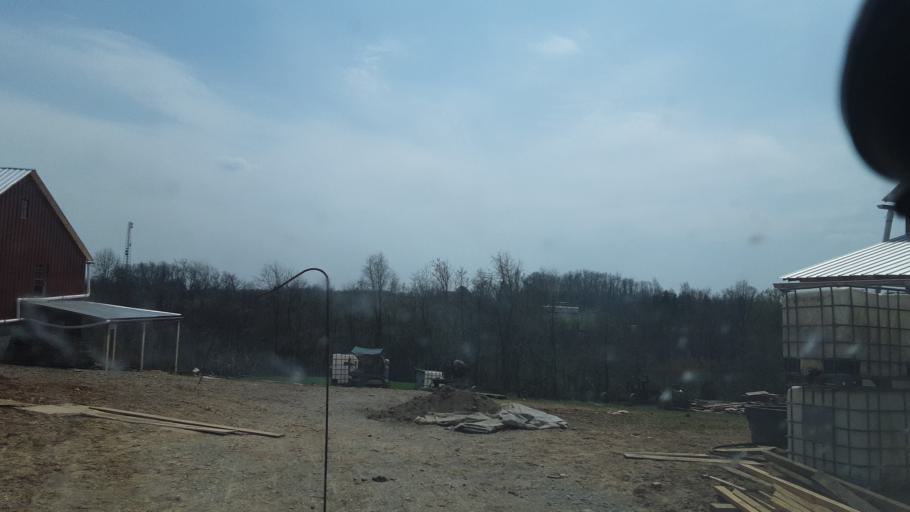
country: US
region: Ohio
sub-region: Morgan County
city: McConnelsville
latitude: 39.5023
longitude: -81.8954
